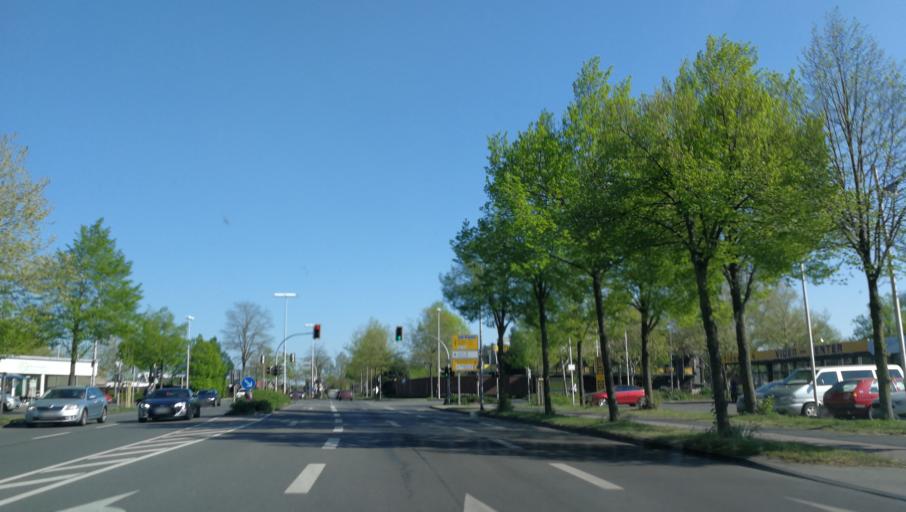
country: DE
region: North Rhine-Westphalia
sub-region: Regierungsbezirk Munster
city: Rheine
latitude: 52.2714
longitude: 7.4426
